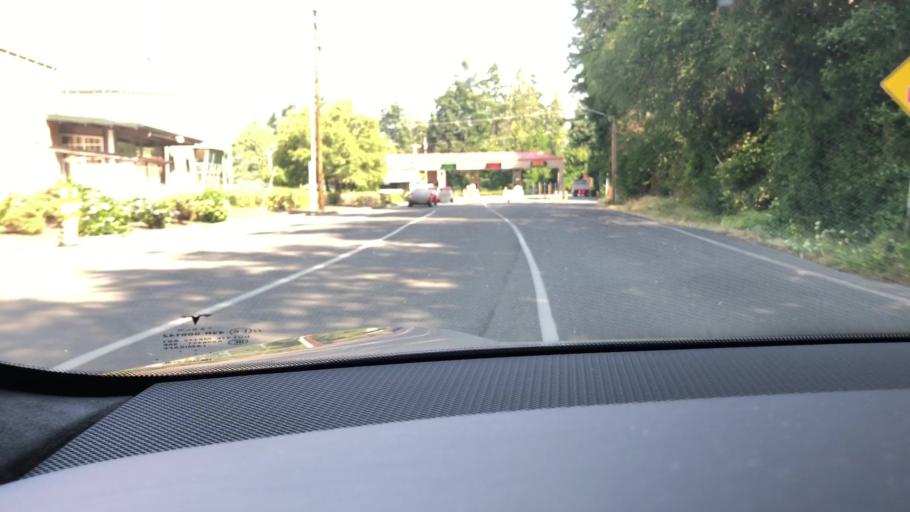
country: US
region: Washington
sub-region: Whatcom County
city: Point Roberts
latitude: 49.0010
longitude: -123.0679
